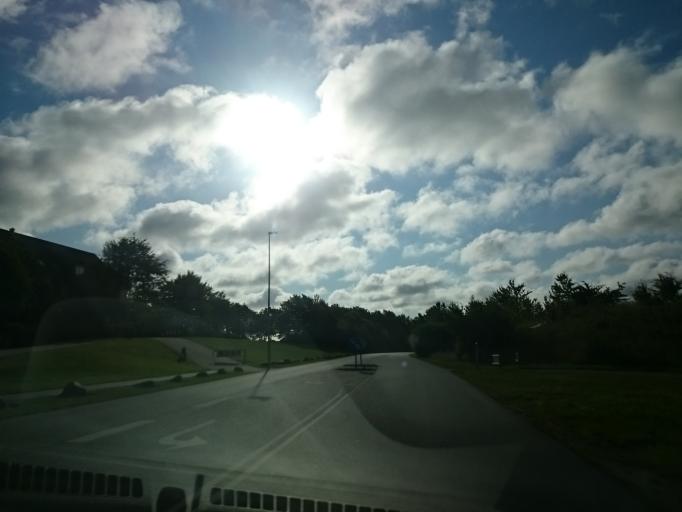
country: DK
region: Central Jutland
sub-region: Arhus Kommune
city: Stavtrup
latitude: 56.1114
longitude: 10.0992
